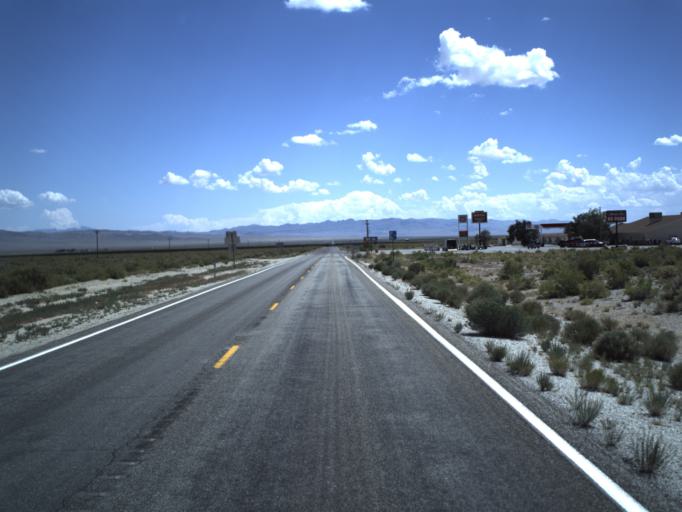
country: US
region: Nevada
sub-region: White Pine County
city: McGill
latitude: 39.0573
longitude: -114.0517
